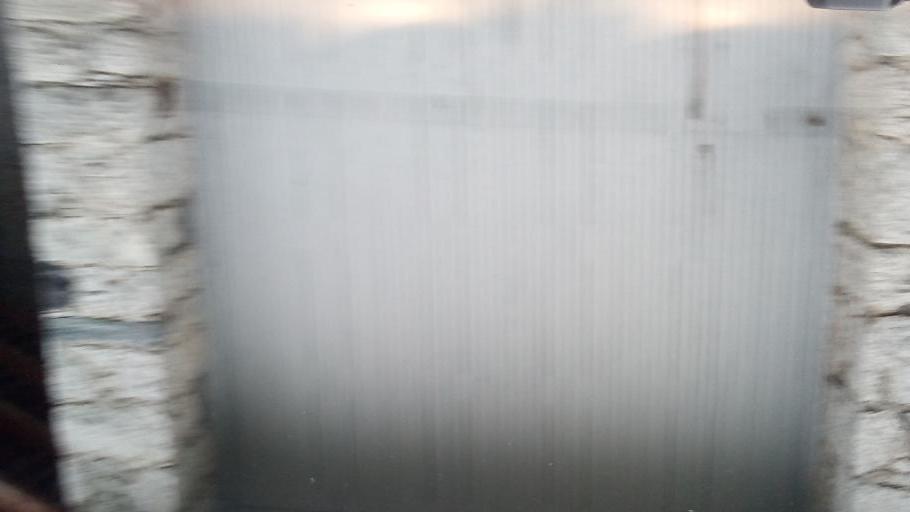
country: FR
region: Midi-Pyrenees
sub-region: Departement des Hautes-Pyrenees
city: Cauterets
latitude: 42.9400
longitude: -0.1782
